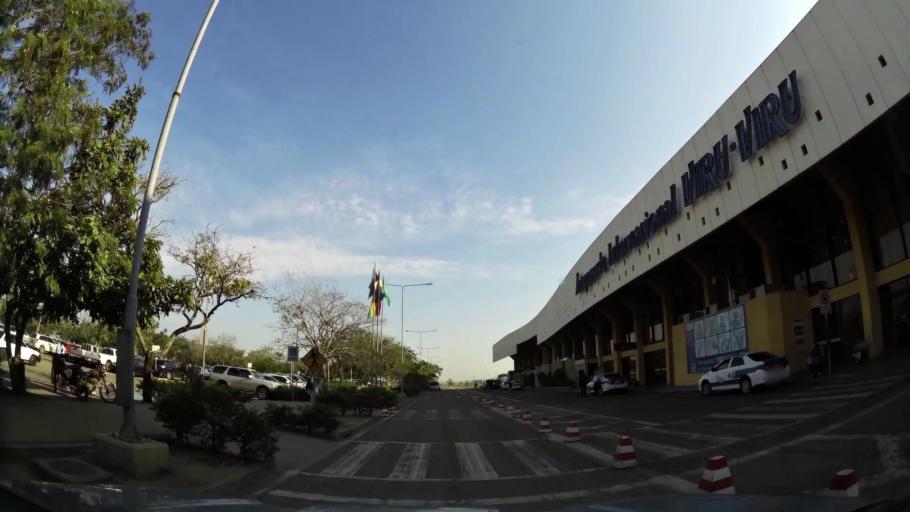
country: BO
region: Santa Cruz
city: La Belgica
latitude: -17.6487
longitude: -63.1400
